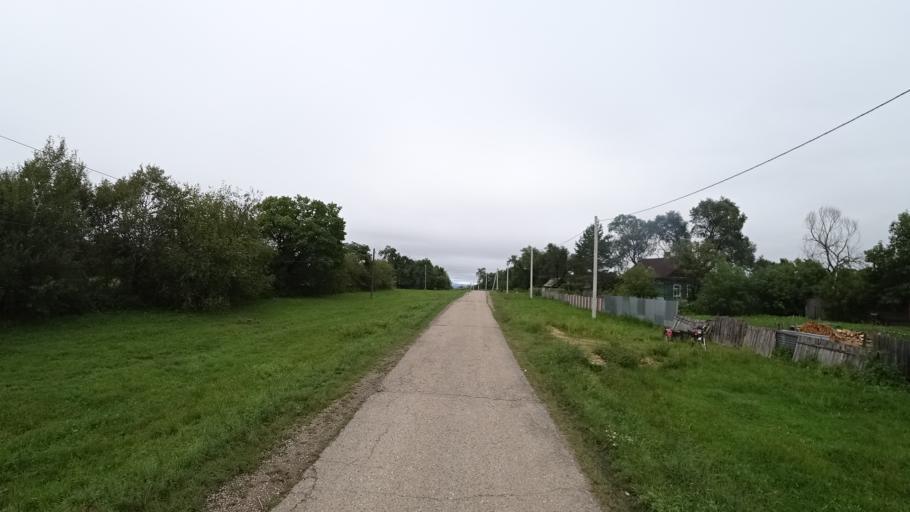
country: RU
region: Primorskiy
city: Monastyrishche
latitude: 44.0789
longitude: 132.5848
